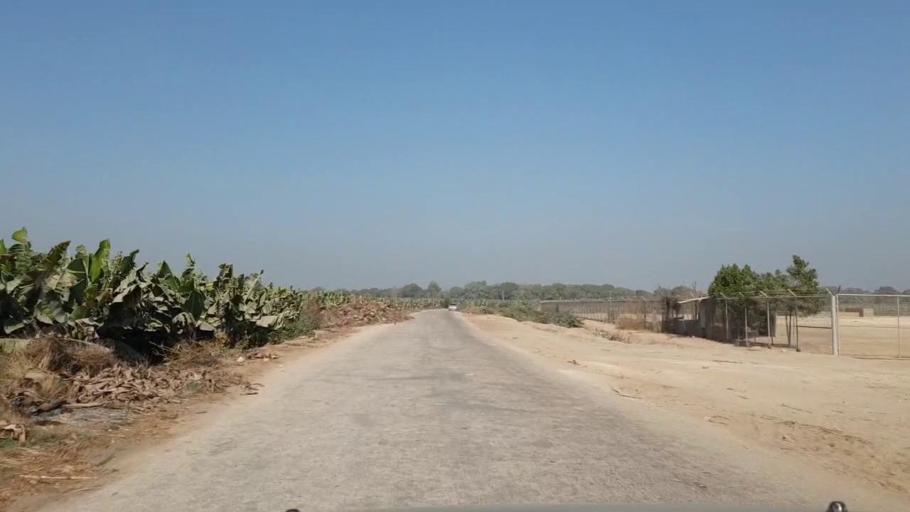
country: PK
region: Sindh
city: Matiari
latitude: 25.6148
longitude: 68.5946
